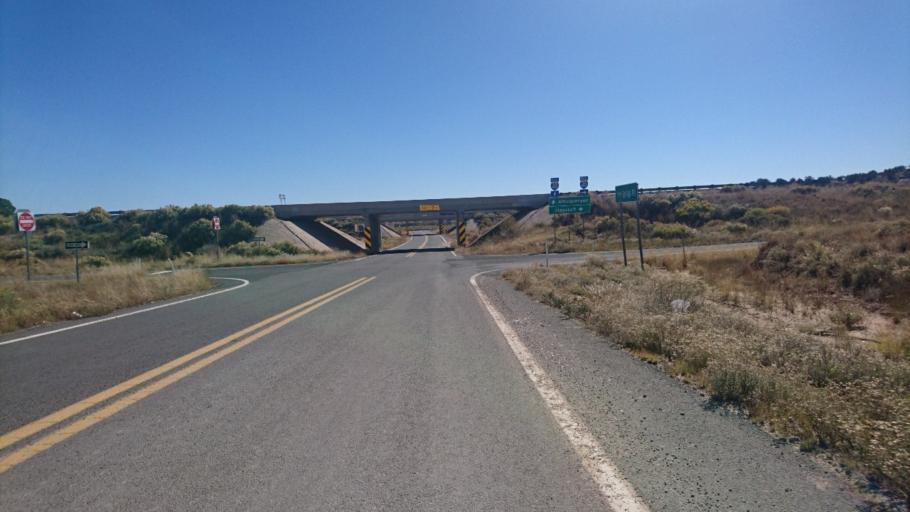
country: US
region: Arizona
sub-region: Apache County
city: Houck
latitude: 35.2829
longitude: -109.2404
